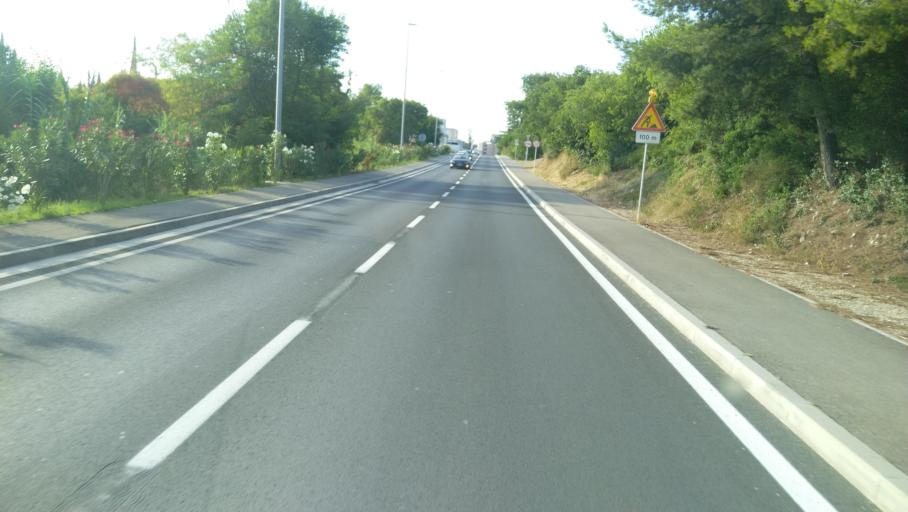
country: HR
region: Sibensko-Kniniska
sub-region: Grad Sibenik
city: Sibenik
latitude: 43.7183
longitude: 15.9105
